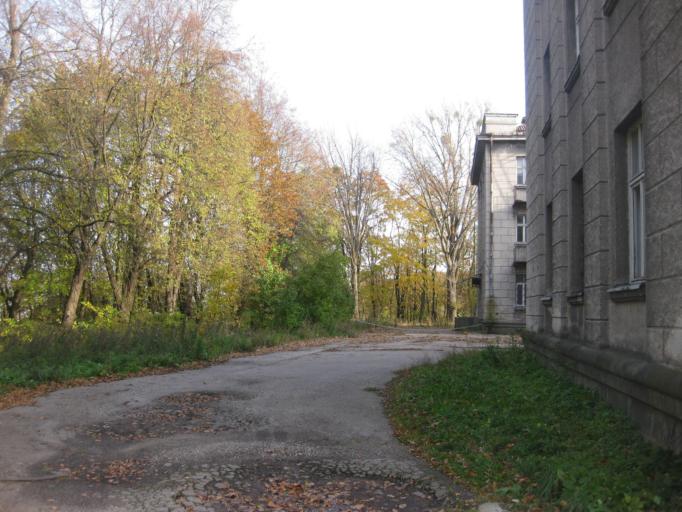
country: LT
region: Kauno apskritis
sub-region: Kaunas
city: Kaunas
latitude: 54.8924
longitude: 23.8802
